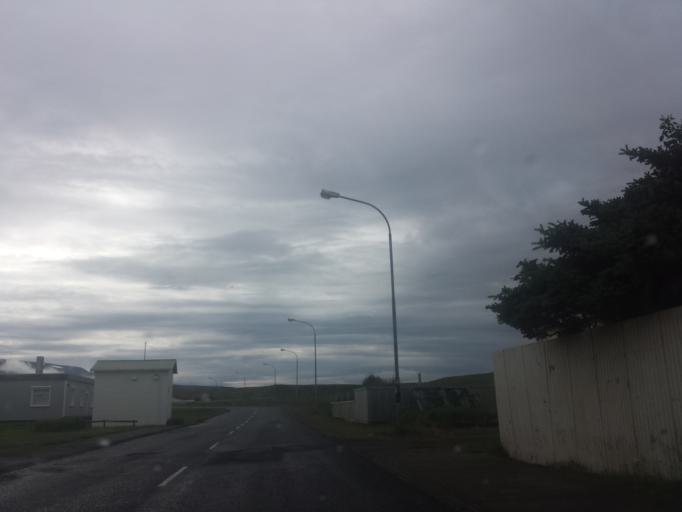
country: IS
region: Northwest
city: Saudarkrokur
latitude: 65.6597
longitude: -20.3004
